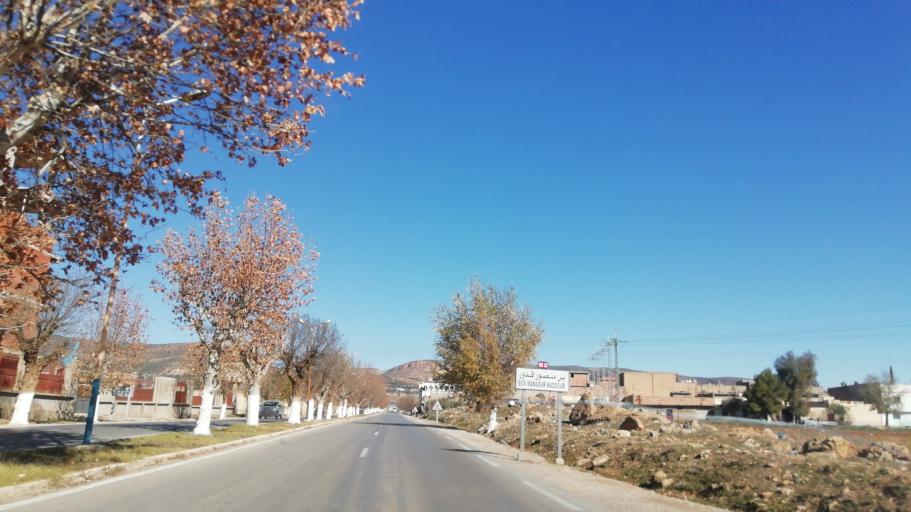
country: DZ
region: Tlemcen
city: Sebdou
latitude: 34.6626
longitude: -1.3223
